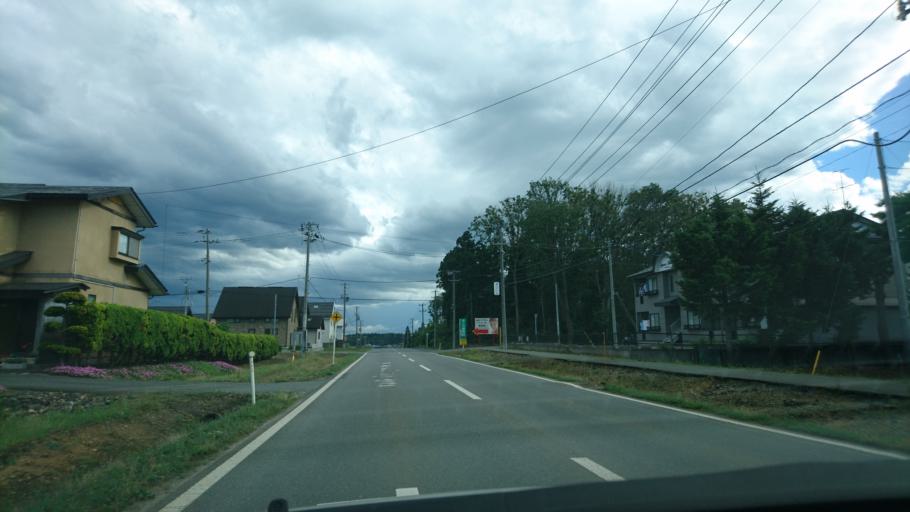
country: JP
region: Iwate
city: Kitakami
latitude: 39.3251
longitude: 141.1275
